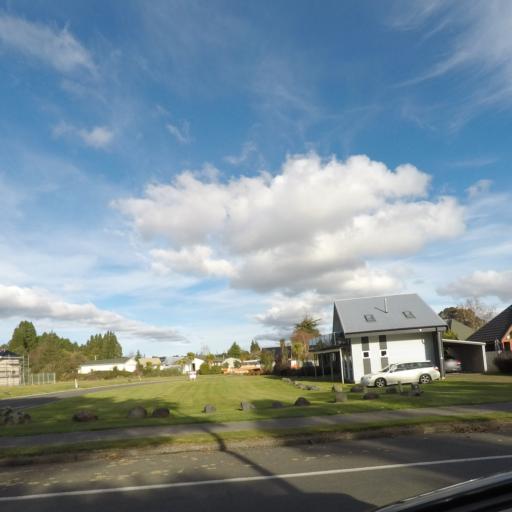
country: NZ
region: Manawatu-Wanganui
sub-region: Ruapehu District
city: Waiouru
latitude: -39.4081
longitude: 175.4085
